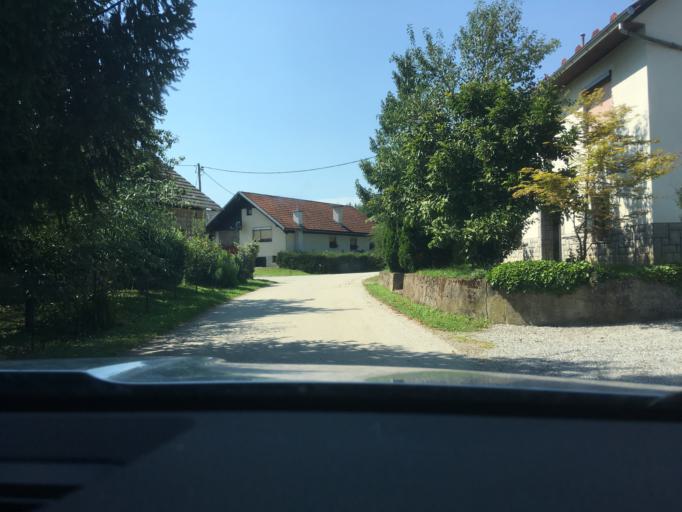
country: SI
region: Metlika
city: Metlika
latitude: 45.6149
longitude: 15.2955
